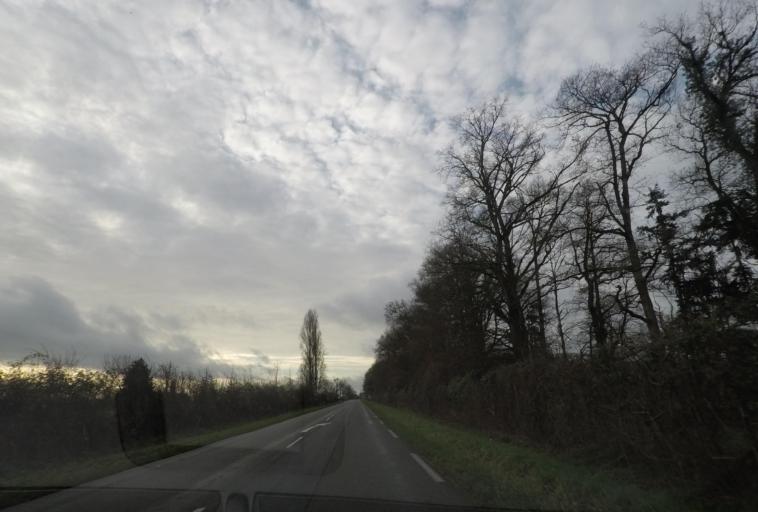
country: FR
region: Pays de la Loire
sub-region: Departement de la Sarthe
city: Saint-Calais
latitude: 47.9463
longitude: 0.7525
